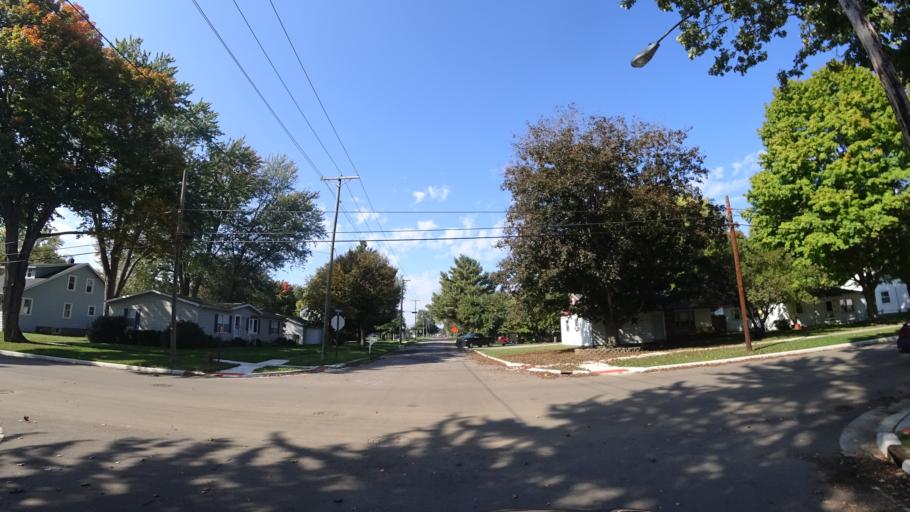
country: US
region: Michigan
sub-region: Saint Joseph County
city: Three Rivers
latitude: 41.9350
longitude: -85.6400
